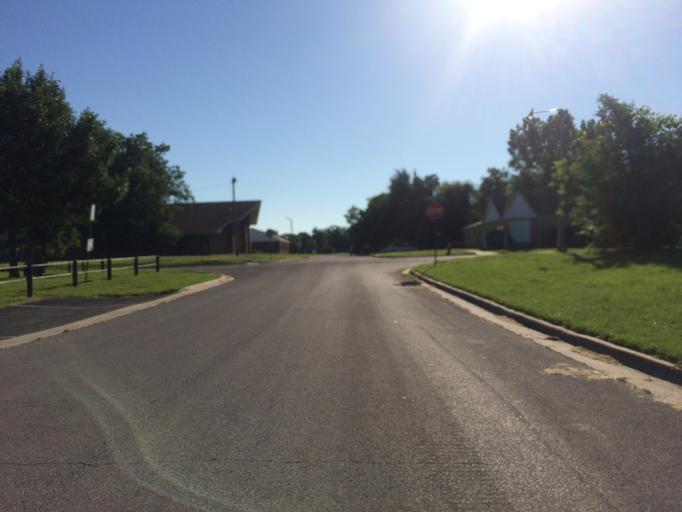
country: US
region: Oklahoma
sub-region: Cleveland County
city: Norman
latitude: 35.2224
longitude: -97.4343
